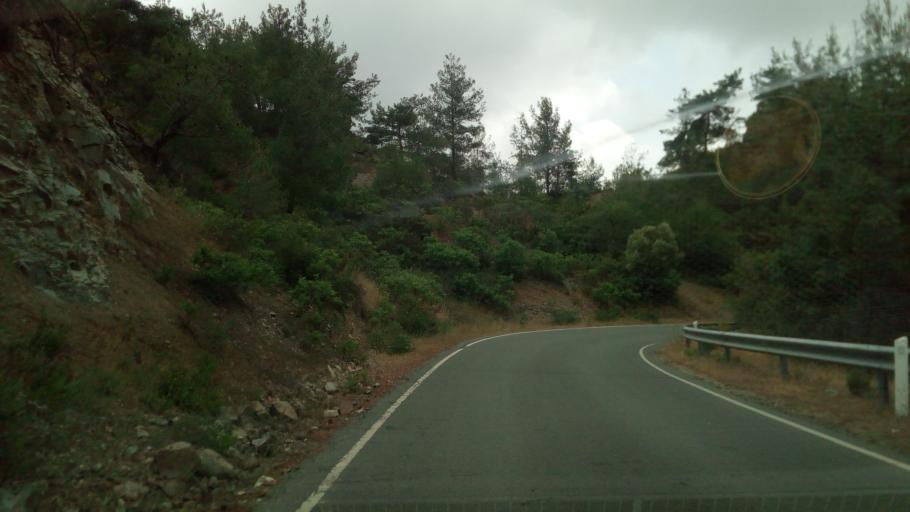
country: CY
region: Limassol
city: Pelendri
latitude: 34.8954
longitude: 32.9959
